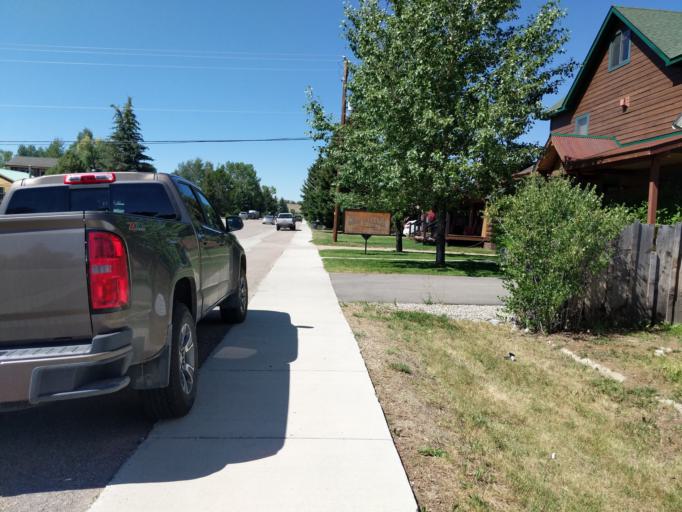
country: US
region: Wyoming
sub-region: Sublette County
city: Pinedale
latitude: 42.8677
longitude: -109.8612
